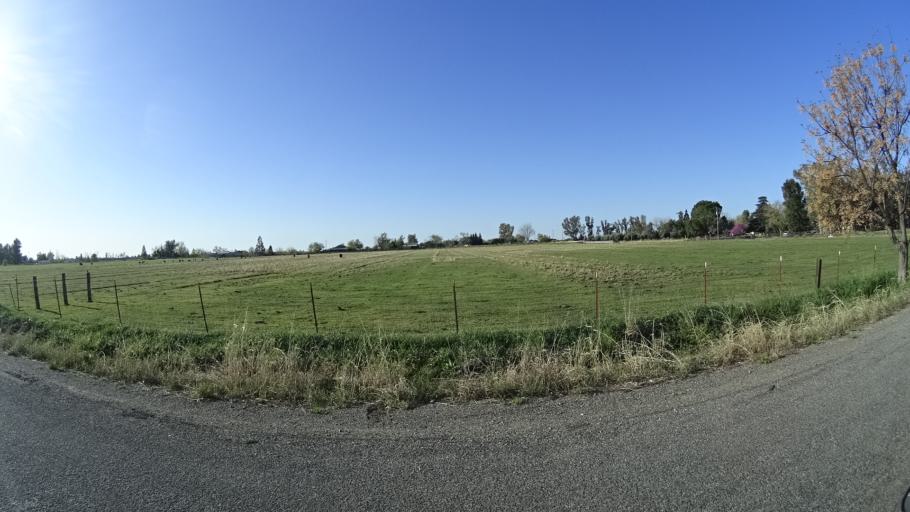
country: US
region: California
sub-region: Glenn County
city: Orland
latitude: 39.7588
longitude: -122.2377
